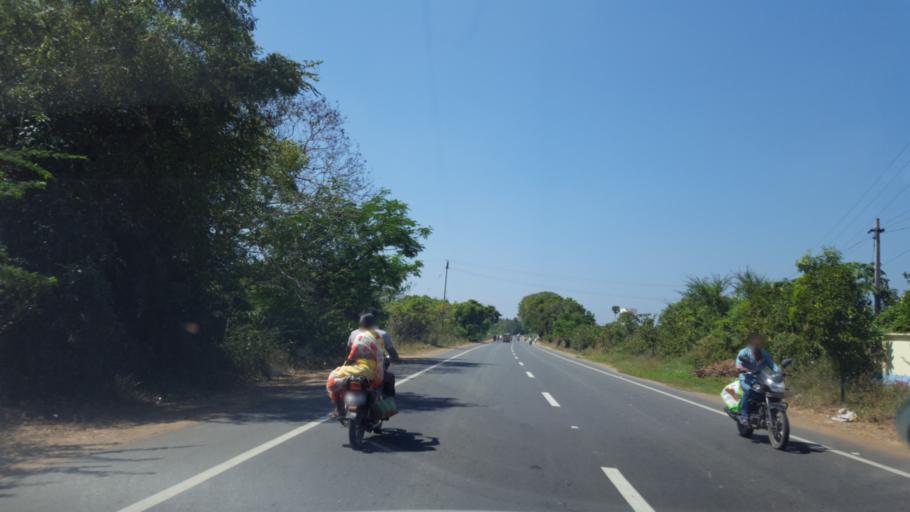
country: IN
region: Tamil Nadu
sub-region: Kancheepuram
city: Karumbakkam
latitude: 12.6371
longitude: 80.0462
